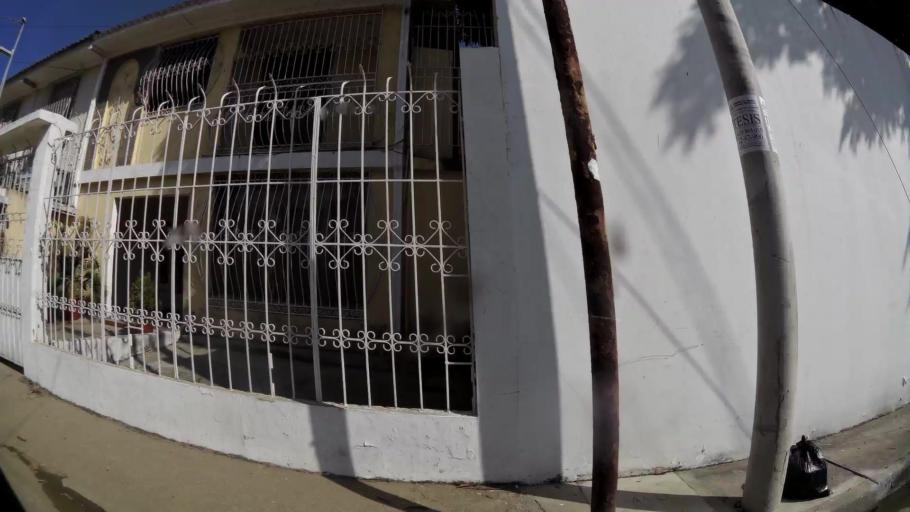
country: EC
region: Guayas
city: Guayaquil
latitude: -2.2293
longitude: -79.8933
